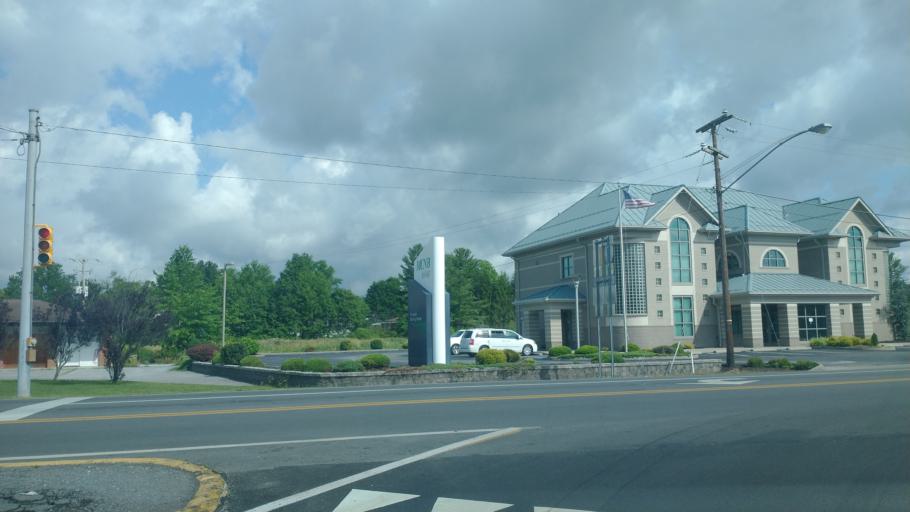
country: US
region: West Virginia
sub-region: Mercer County
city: Princeton
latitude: 37.3607
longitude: -81.1054
